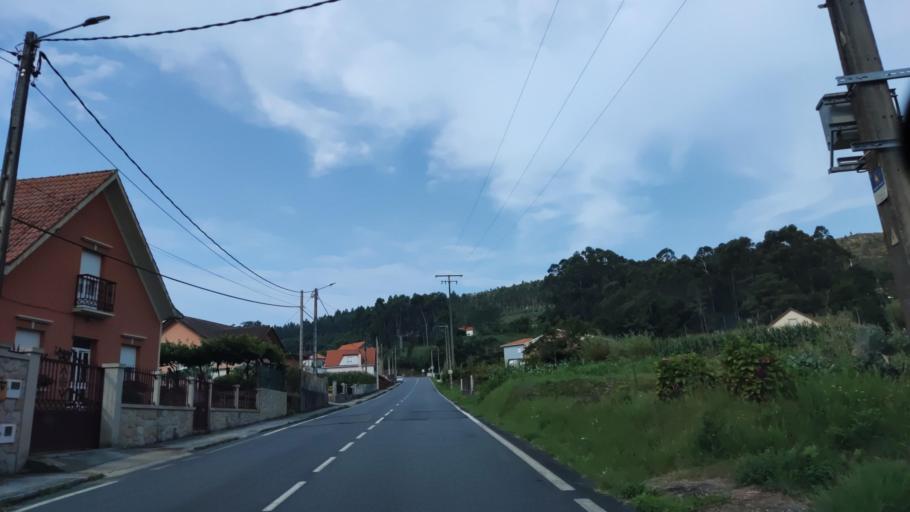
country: ES
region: Galicia
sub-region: Provincia da Coruna
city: Rianxo
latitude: 42.6541
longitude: -8.7737
